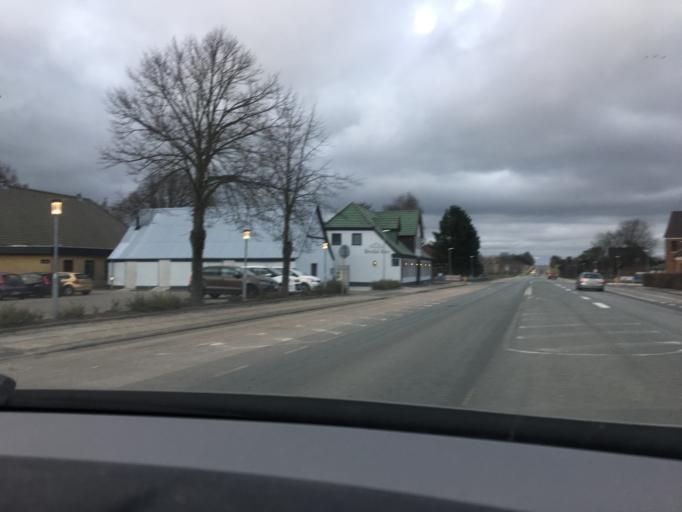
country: DK
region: Central Jutland
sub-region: Hedensted Kommune
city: Hedensted
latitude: 55.7476
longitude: 9.6416
